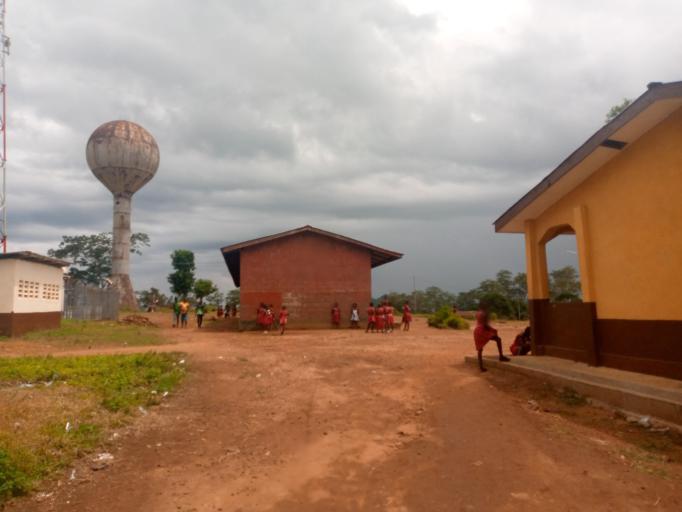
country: SL
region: Southern Province
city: Mogbwemo
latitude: 7.6023
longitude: -12.1731
